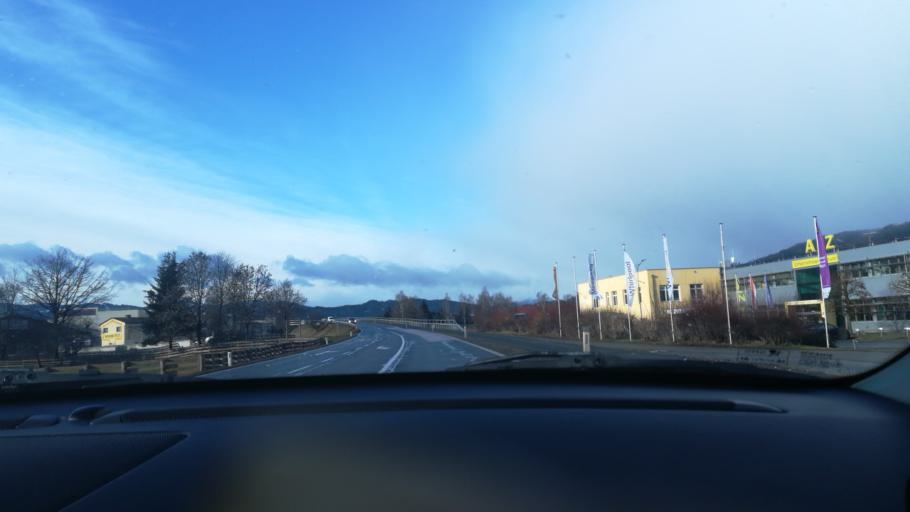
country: AT
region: Styria
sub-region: Politischer Bezirk Murtal
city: Zeltweg
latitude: 47.1954
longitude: 14.7318
